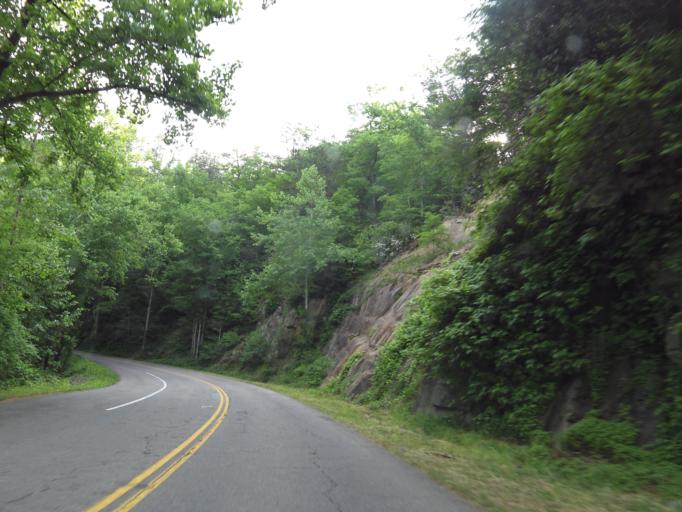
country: US
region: Tennessee
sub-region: Sevier County
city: Gatlinburg
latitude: 35.6644
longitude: -83.6220
